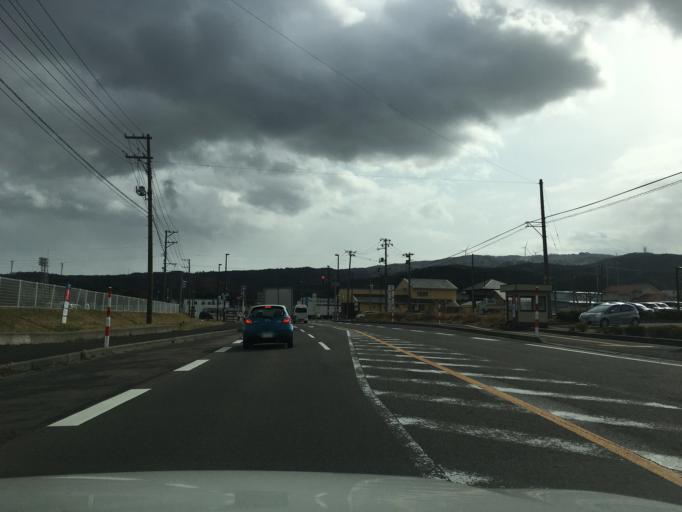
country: JP
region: Yamagata
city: Yuza
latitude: 39.2855
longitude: 139.9611
